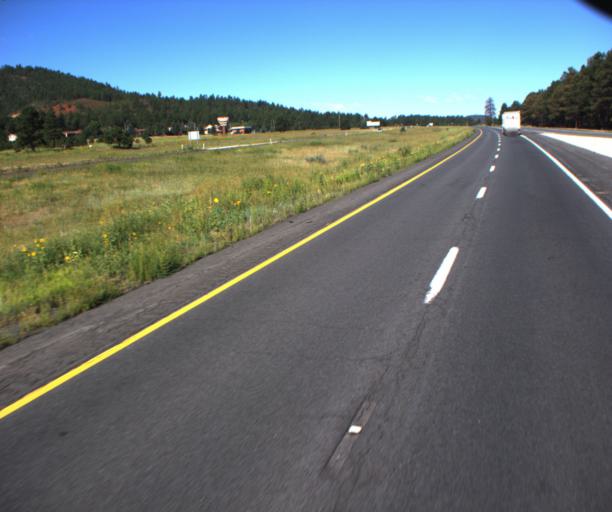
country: US
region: Arizona
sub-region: Coconino County
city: Parks
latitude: 35.2650
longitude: -112.0519
